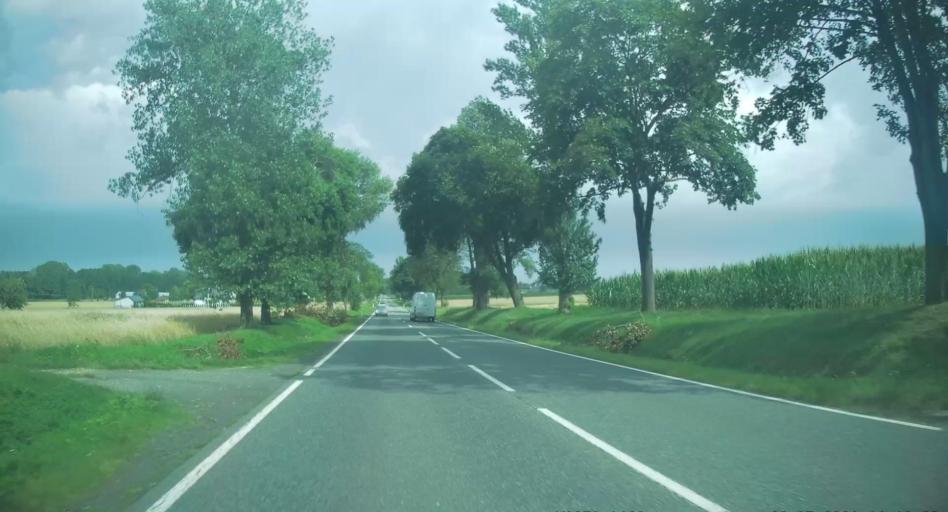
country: PL
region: Lodz Voivodeship
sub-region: Powiat brzezinski
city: Jezow
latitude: 51.8097
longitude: 20.0025
